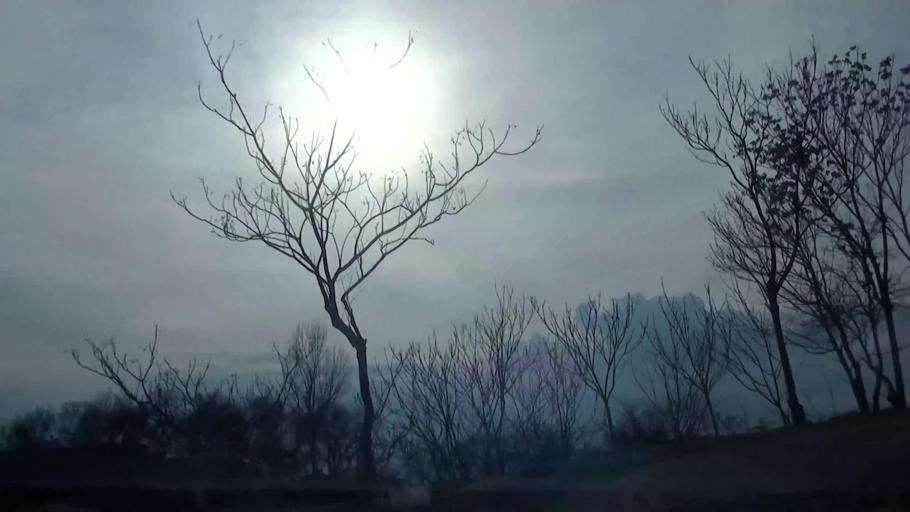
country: PK
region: Azad Kashmir
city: Muzaffarabad
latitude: 34.3670
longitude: 73.5257
